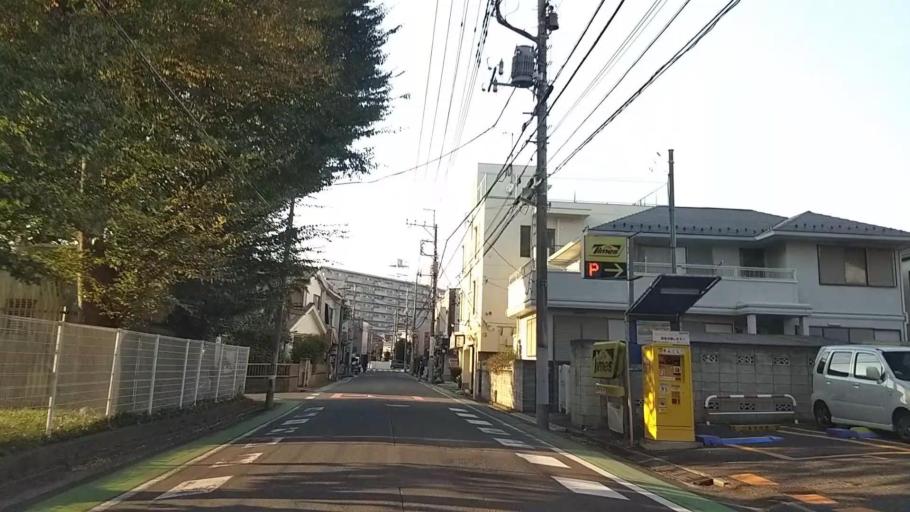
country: JP
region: Saitama
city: Tokorozawa
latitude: 35.8074
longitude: 139.4538
